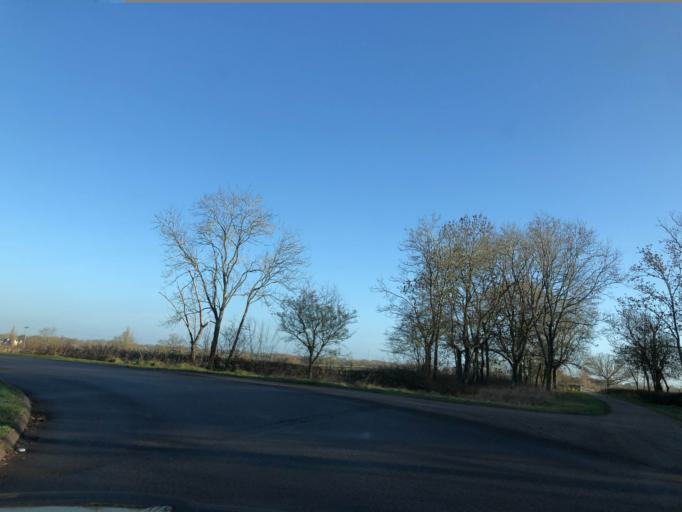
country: GB
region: England
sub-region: Warwickshire
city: Wellesbourne Mountford
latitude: 52.1912
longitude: -1.5143
